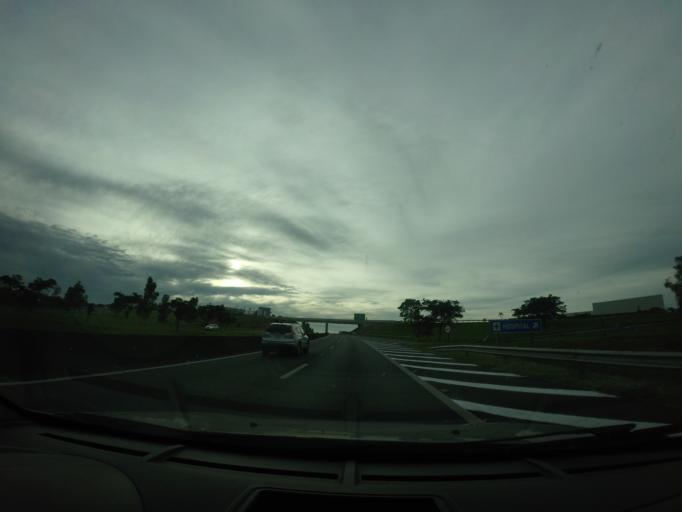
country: BR
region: Sao Paulo
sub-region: Itatiba
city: Itatiba
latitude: -22.9749
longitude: -46.8354
